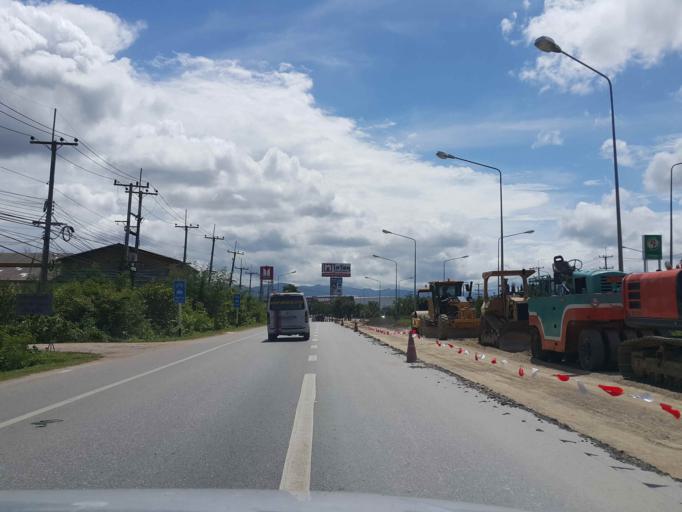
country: TH
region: Tak
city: Tak
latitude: 16.8530
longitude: 99.1177
